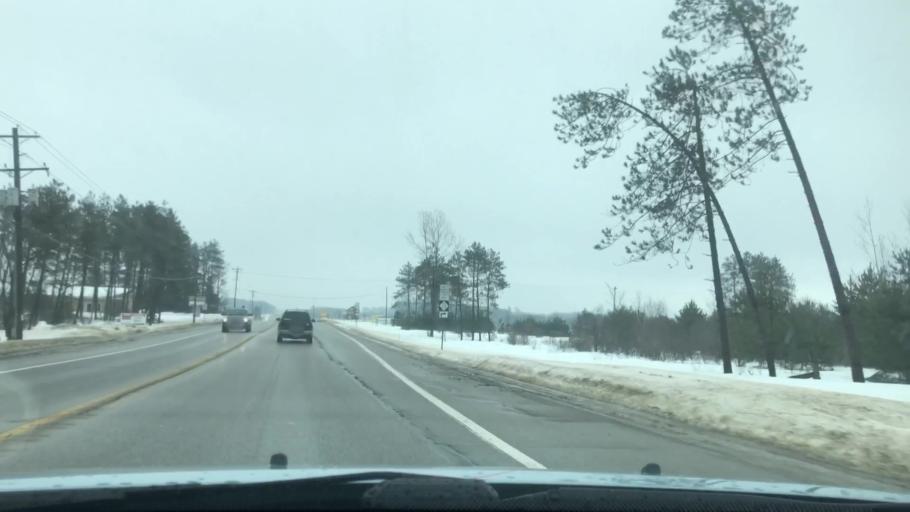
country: US
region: Michigan
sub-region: Otsego County
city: Gaylord
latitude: 45.0275
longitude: -84.7294
